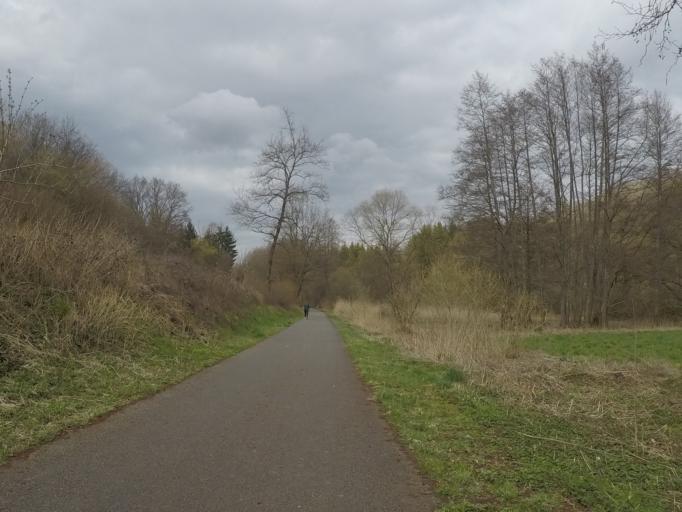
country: DE
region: Rheinland-Pfalz
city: Dellfeld
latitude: 49.2344
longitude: 7.4605
